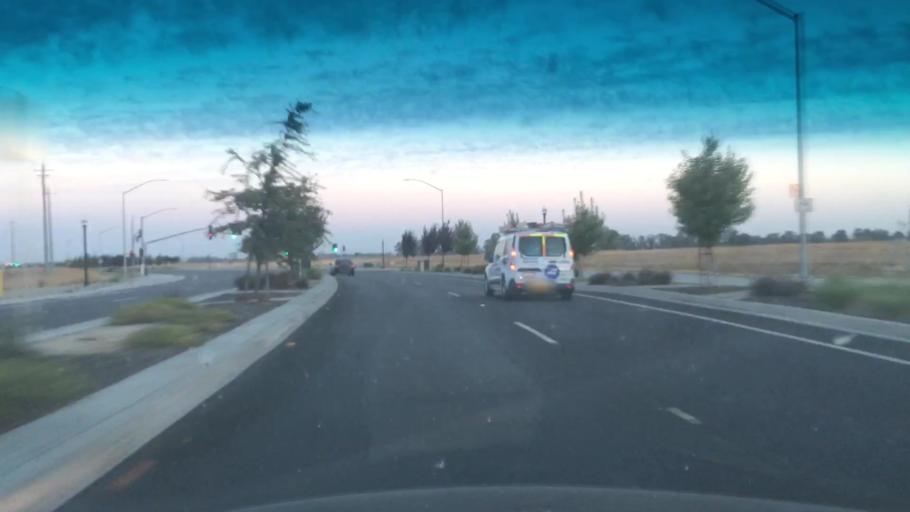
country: US
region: California
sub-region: Sacramento County
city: Parkway
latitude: 38.4631
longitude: -121.4666
